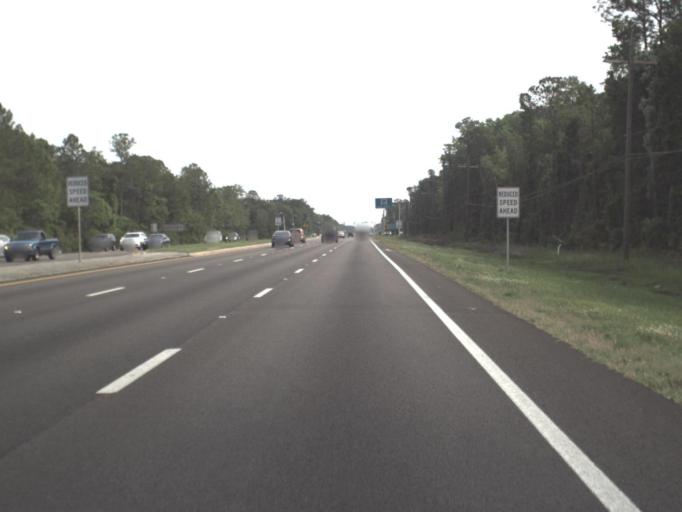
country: US
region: Florida
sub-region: Saint Johns County
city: Fruit Cove
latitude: 30.0981
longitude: -81.7057
